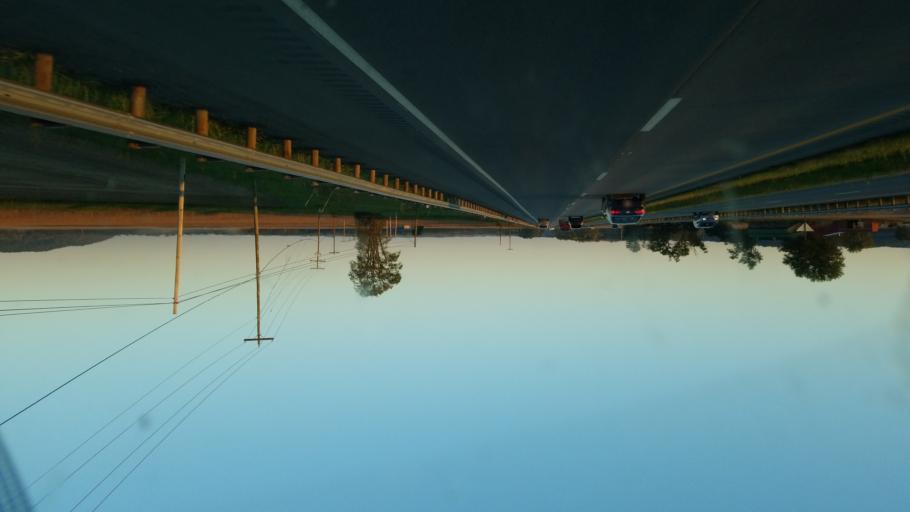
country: US
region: Ohio
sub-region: Pike County
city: Piketon
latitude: 39.0753
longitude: -83.0047
